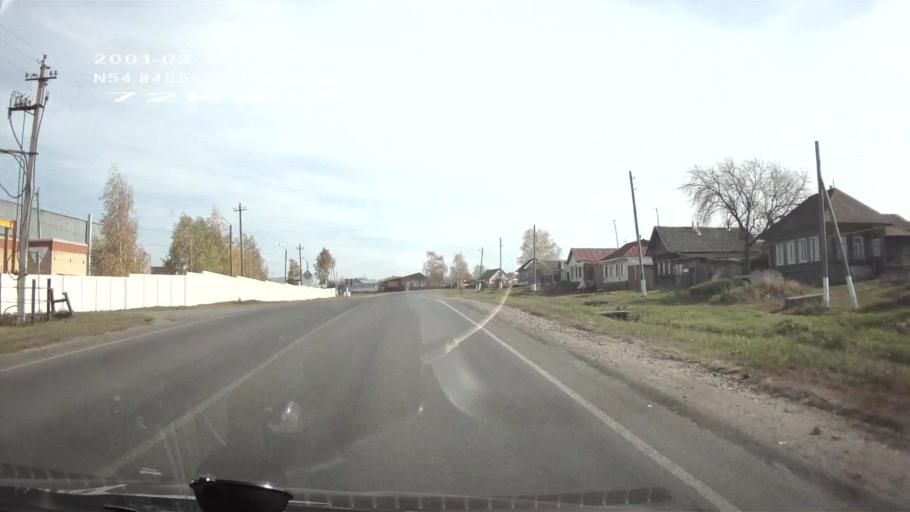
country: RU
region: Mordoviya
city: Turgenevo
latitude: 54.8454
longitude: 46.3443
